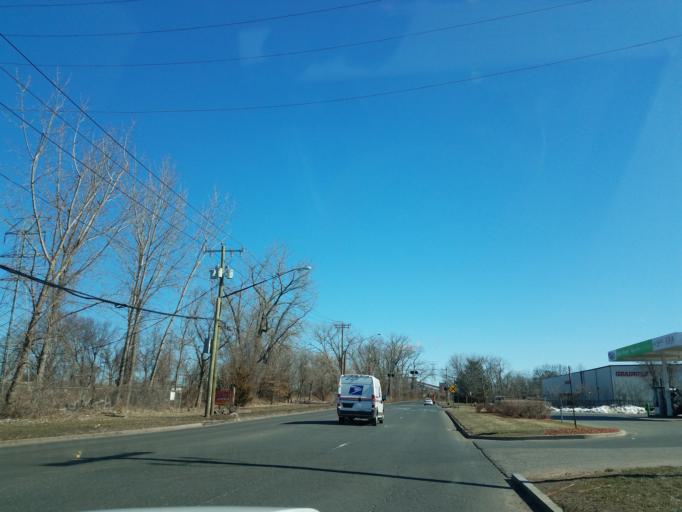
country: US
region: Connecticut
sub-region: Hartford County
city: Wethersfield
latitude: 41.7418
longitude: -72.6594
